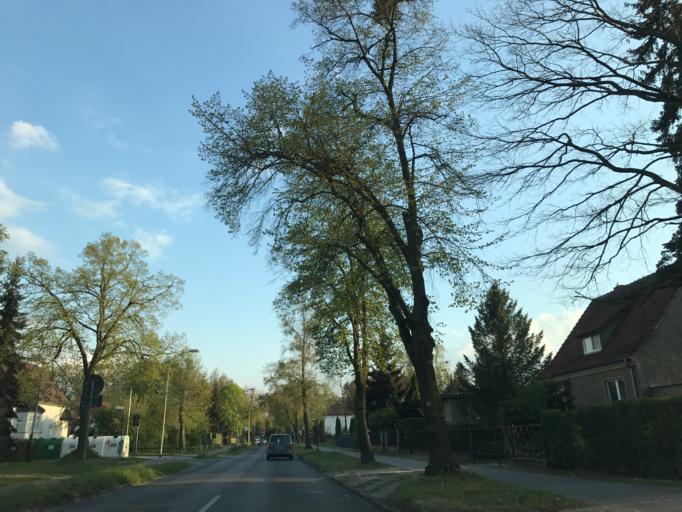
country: DE
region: Brandenburg
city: Dallgow-Doeberitz
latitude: 52.5619
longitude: 13.0502
